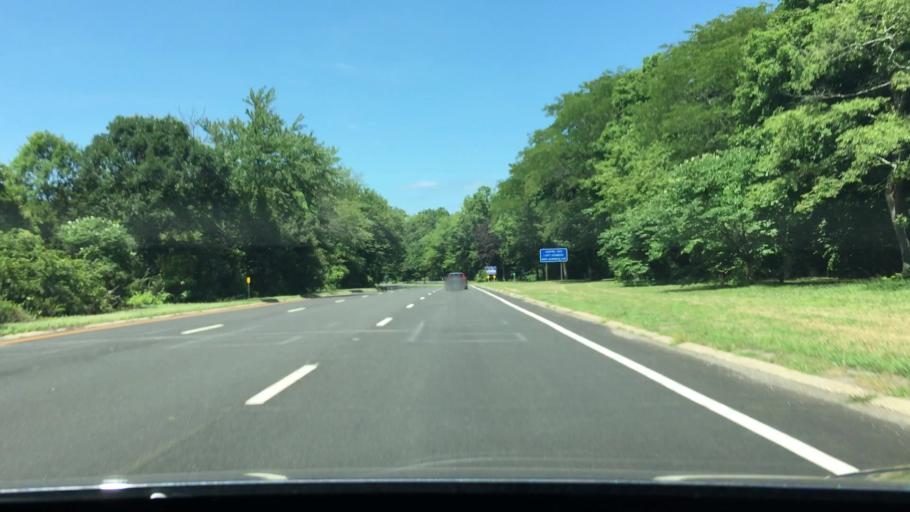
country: US
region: New York
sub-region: Nassau County
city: Wantagh
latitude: 40.6751
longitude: -73.5132
